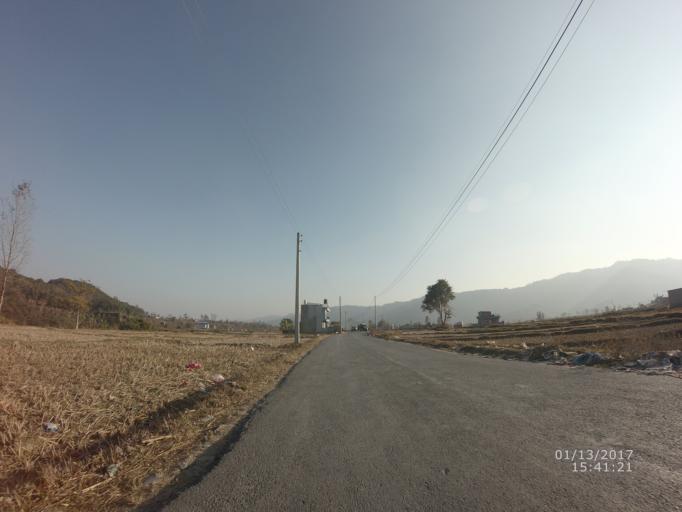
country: NP
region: Western Region
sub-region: Gandaki Zone
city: Pokhara
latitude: 28.1871
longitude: 83.9848
